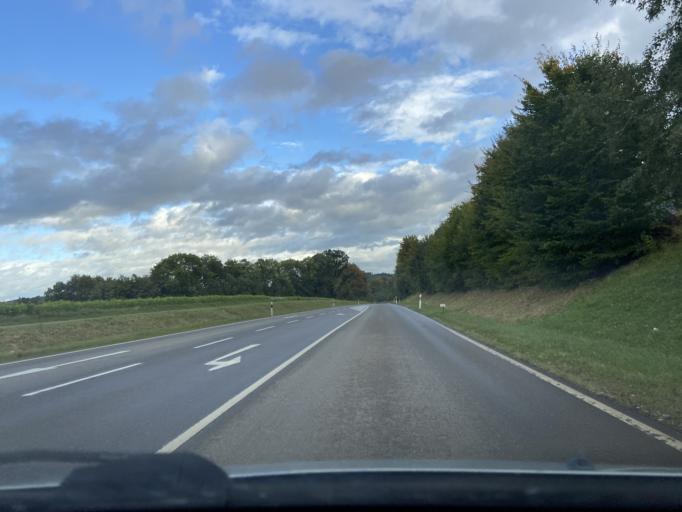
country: DE
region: Baden-Wuerttemberg
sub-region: Tuebingen Region
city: Bingen
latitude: 48.1061
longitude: 9.2640
